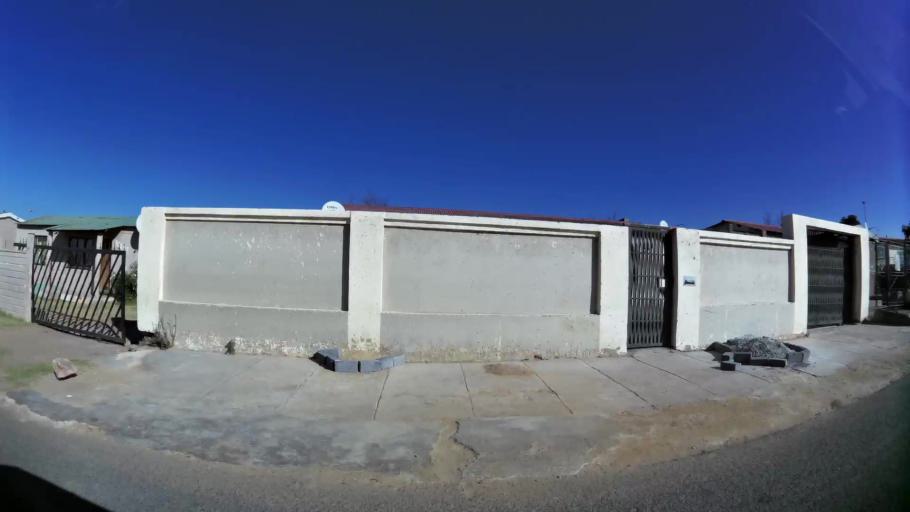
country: ZA
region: Gauteng
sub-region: City of Johannesburg Metropolitan Municipality
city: Soweto
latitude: -26.2230
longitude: 27.9183
